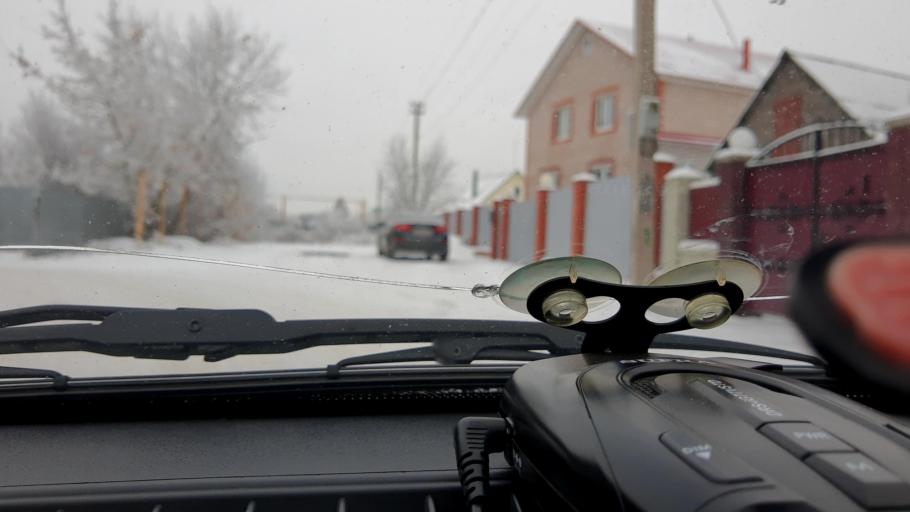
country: RU
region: Bashkortostan
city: Iglino
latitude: 54.7828
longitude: 56.2344
